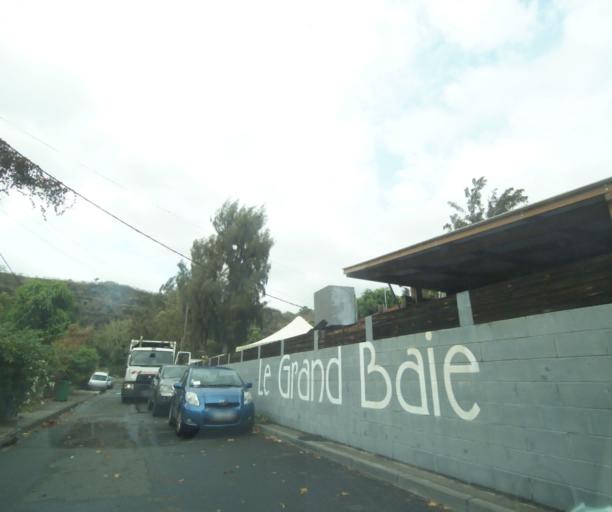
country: RE
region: Reunion
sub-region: Reunion
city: Saint-Paul
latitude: -21.0138
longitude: 55.2613
